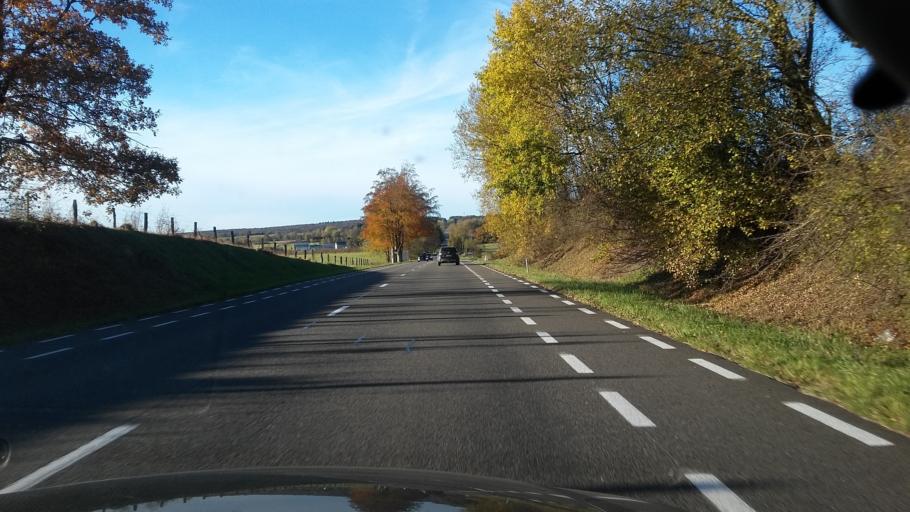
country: BE
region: Wallonia
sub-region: Province du Luxembourg
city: Florenville
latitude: 49.7189
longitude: 5.2482
